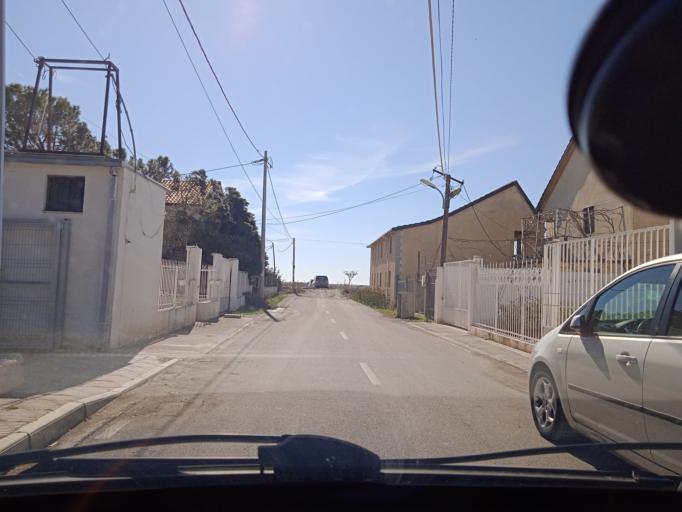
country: AL
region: Shkoder
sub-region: Rrethi i Shkodres
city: Velipoje
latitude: 41.8636
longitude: 19.4117
